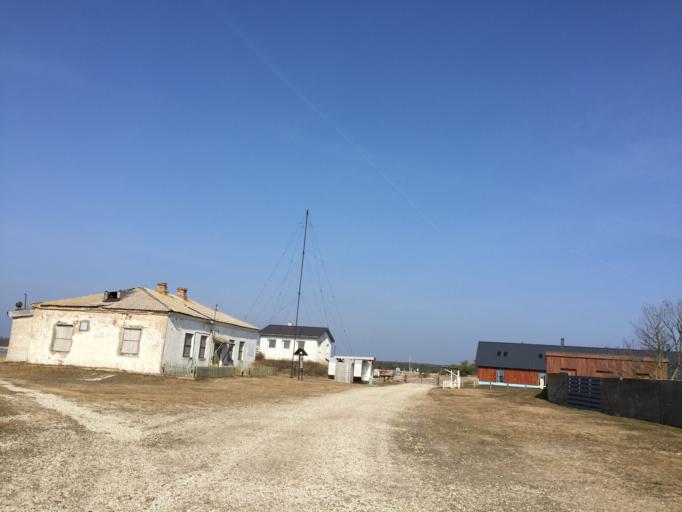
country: LV
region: Dundaga
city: Dundaga
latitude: 57.9104
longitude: 22.0552
